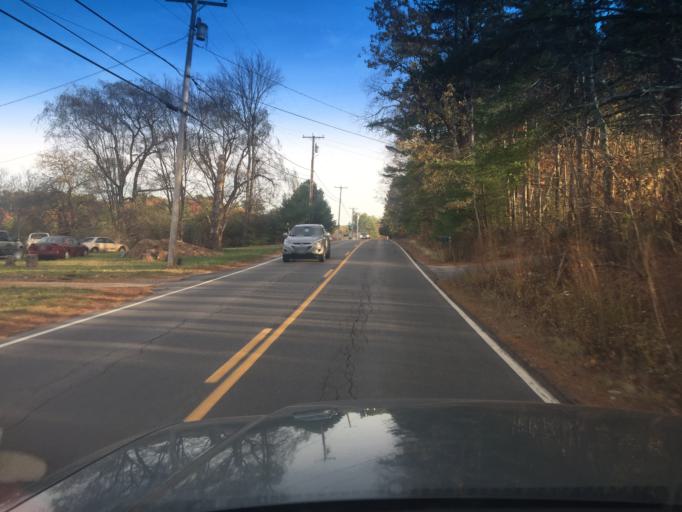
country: US
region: Maine
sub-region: York County
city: Eliot
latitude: 43.1821
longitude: -70.7382
